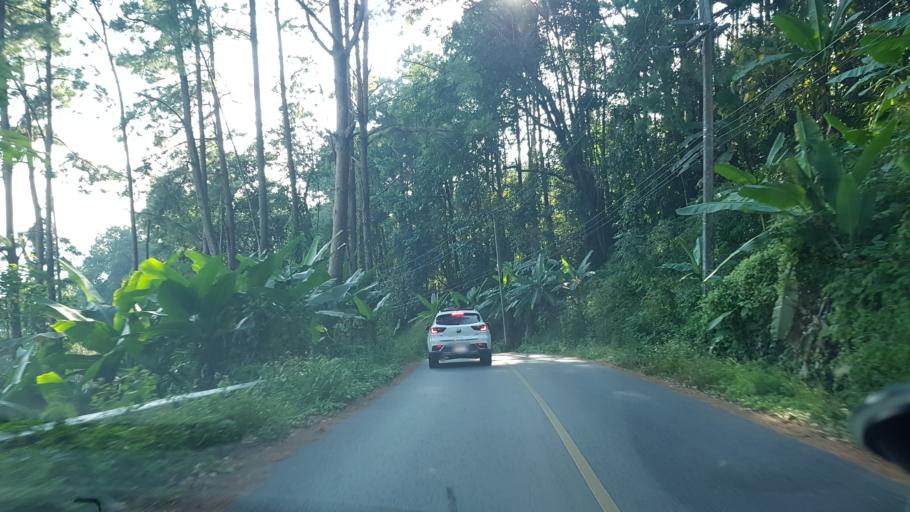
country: TH
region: Chiang Rai
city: Mae Fa Luang
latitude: 20.3205
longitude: 99.8214
